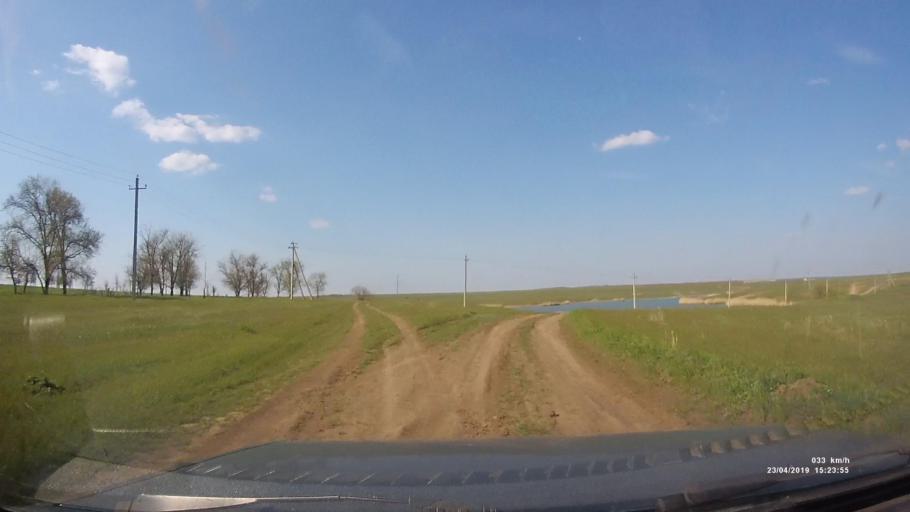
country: RU
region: Rostov
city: Remontnoye
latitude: 46.5383
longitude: 42.9695
